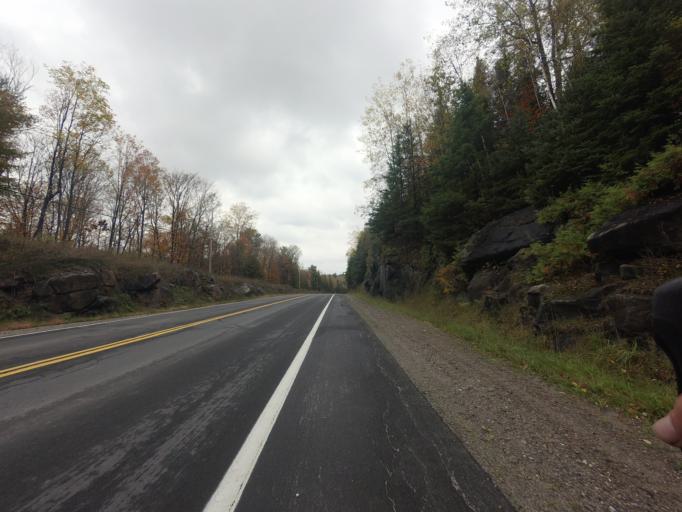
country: CA
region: Ontario
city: Perth
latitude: 45.1141
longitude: -76.4864
